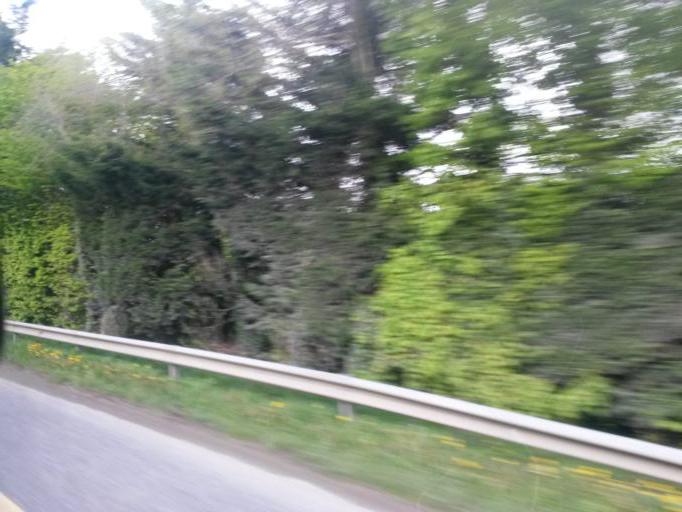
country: IE
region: Leinster
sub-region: Loch Garman
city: Enniscorthy
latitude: 52.4738
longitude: -6.5620
